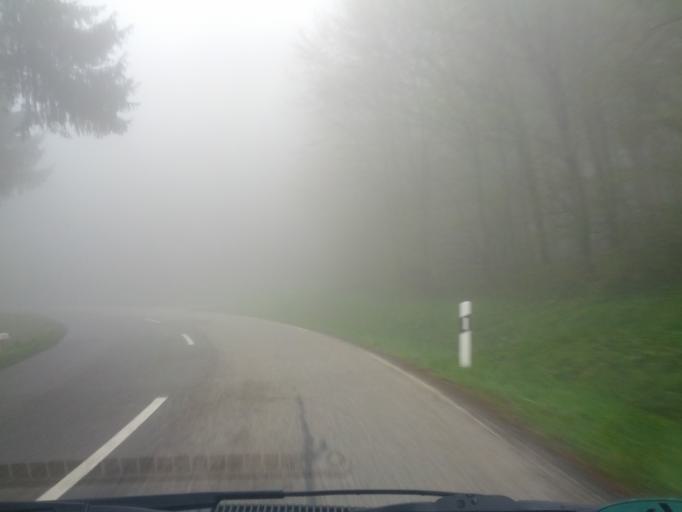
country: DE
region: Baden-Wuerttemberg
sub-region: Freiburg Region
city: Rickenbach
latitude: 47.6155
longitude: 7.9652
